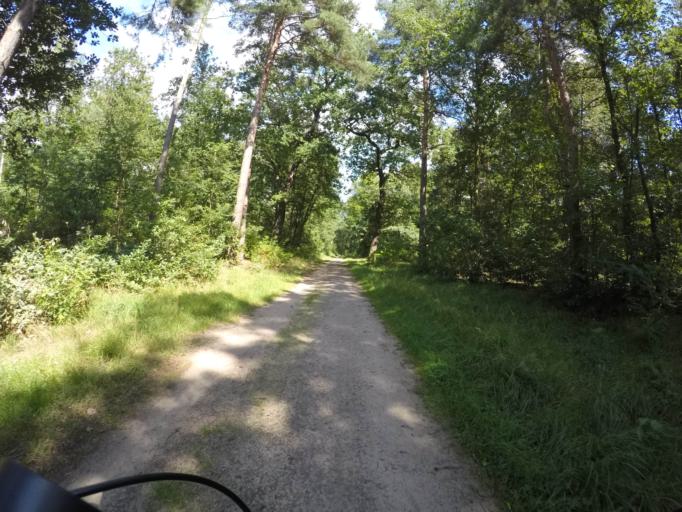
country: DE
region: Brandenburg
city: Potsdam
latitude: 52.3920
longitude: 13.0035
